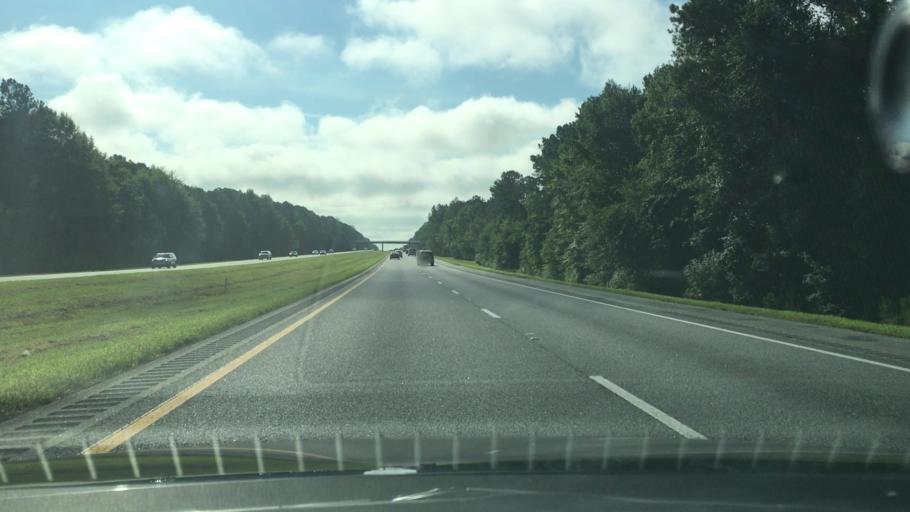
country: US
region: Georgia
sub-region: Walton County
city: Social Circle
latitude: 33.5889
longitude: -83.6180
